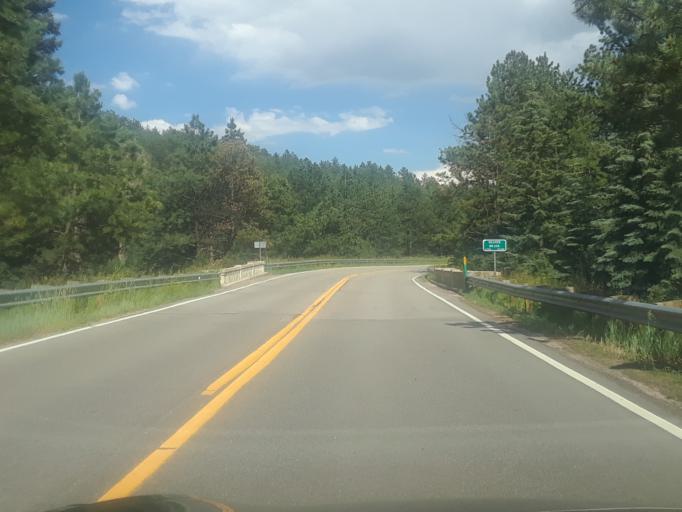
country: US
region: Colorado
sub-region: Jefferson County
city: Kittredge
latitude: 39.7184
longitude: -105.3684
